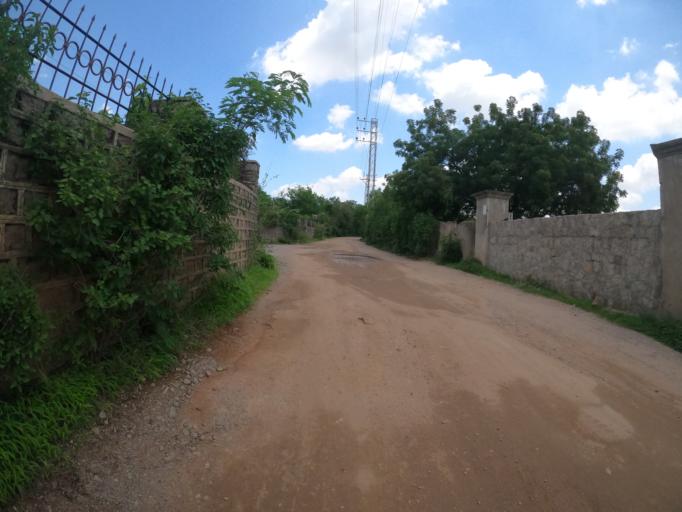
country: IN
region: Telangana
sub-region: Medak
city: Serilingampalle
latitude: 17.3731
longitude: 78.3248
